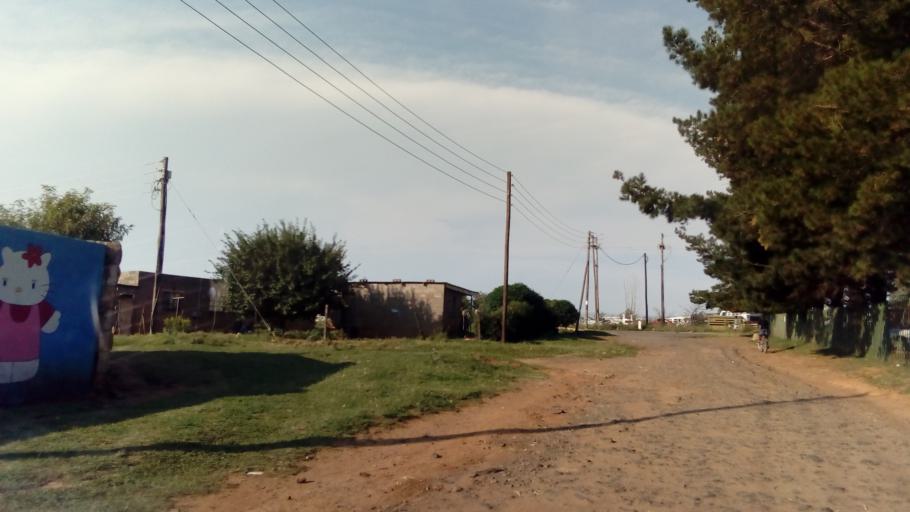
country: LS
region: Maseru
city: Maseru
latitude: -29.2949
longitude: 27.5320
